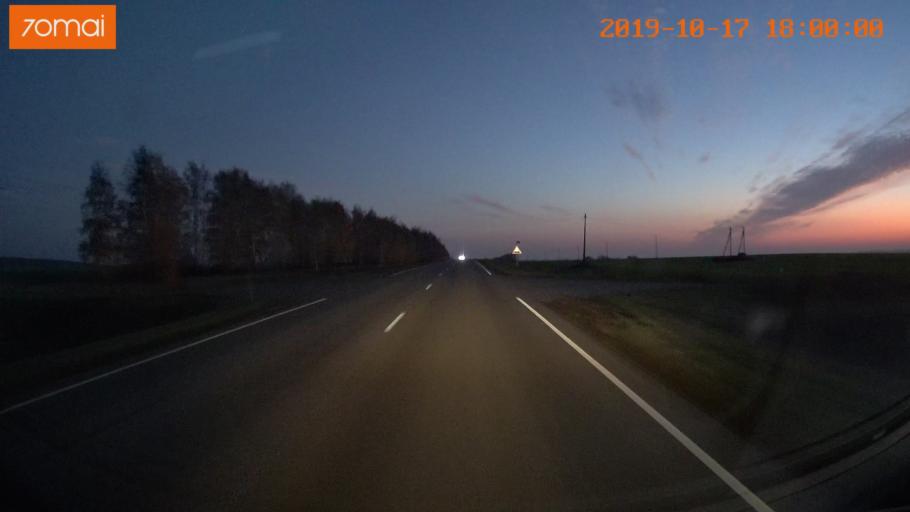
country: RU
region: Tula
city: Kurkino
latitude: 53.5285
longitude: 38.6181
